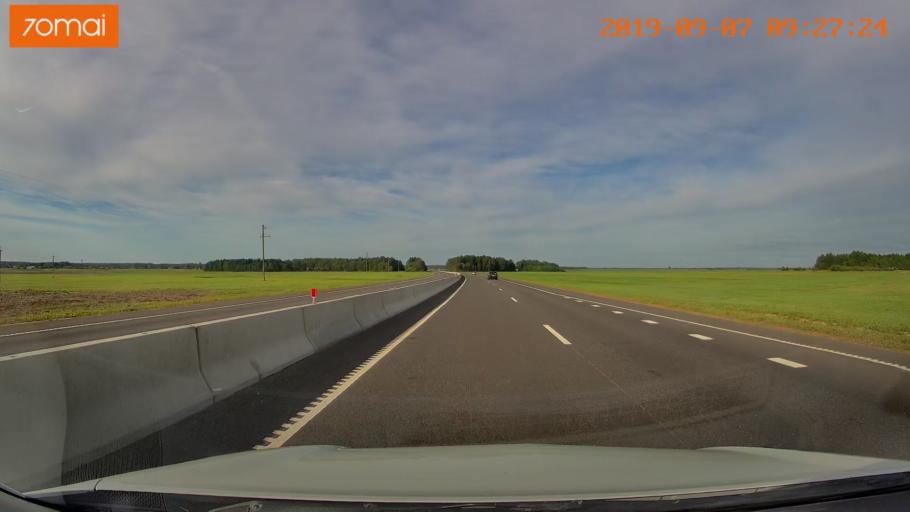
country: BY
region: Grodnenskaya
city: Lyubcha
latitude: 53.9129
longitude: 26.0777
